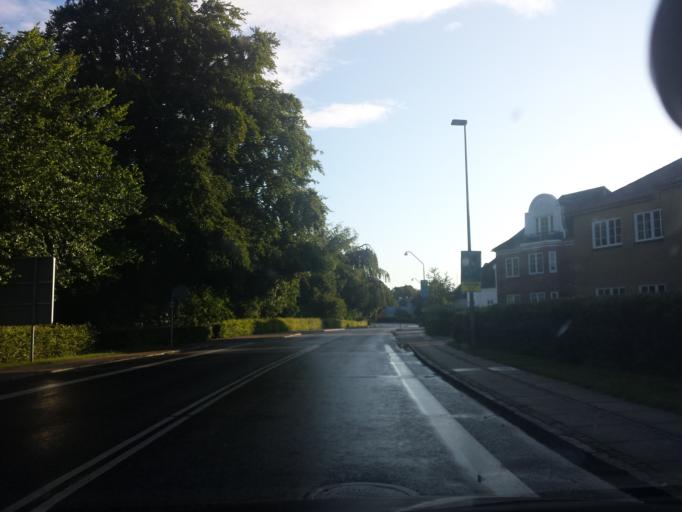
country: DK
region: South Denmark
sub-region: Sonderborg Kommune
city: Grasten
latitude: 54.9176
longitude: 9.5899
